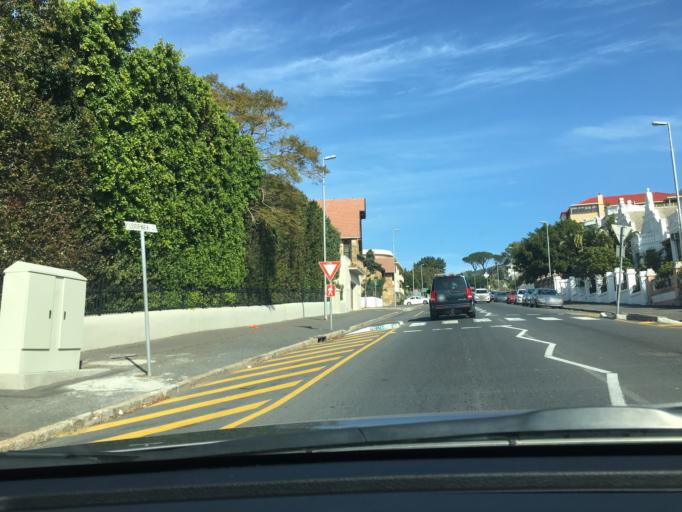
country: ZA
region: Western Cape
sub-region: City of Cape Town
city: Cape Town
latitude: -33.9310
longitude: 18.4068
